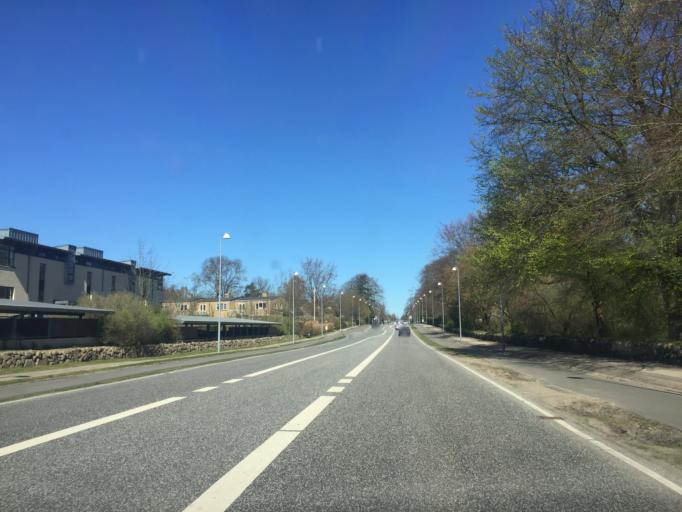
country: DK
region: Capital Region
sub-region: Lyngby-Tarbaek Kommune
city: Kongens Lyngby
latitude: 55.7806
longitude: 12.4928
